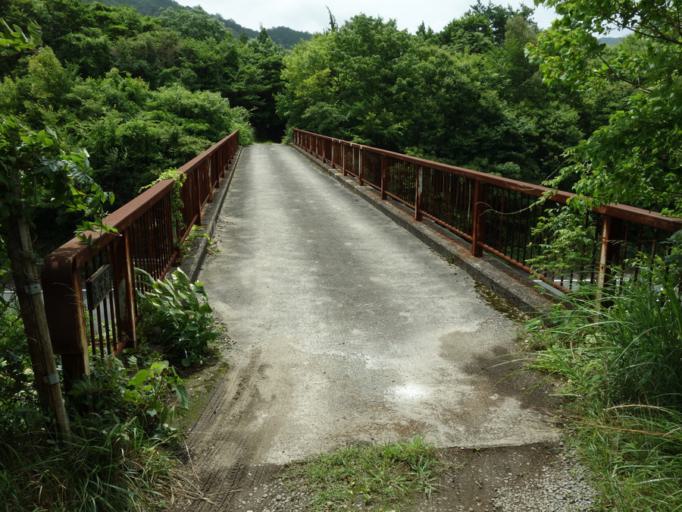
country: JP
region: Yamaguchi
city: Yamaguchi-shi
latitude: 34.1422
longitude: 131.4718
